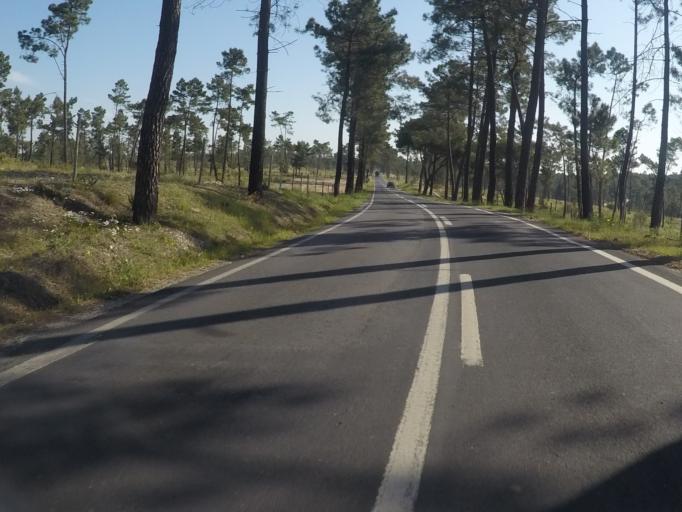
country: PT
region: Setubal
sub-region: Seixal
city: Arrentela
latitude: 38.5363
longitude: -9.1178
